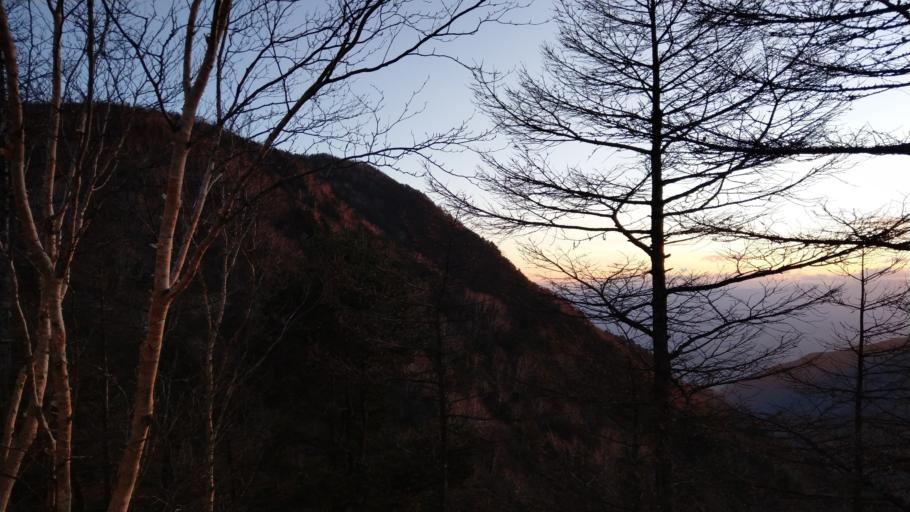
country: JP
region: Nagano
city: Komoro
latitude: 36.4099
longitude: 138.4596
